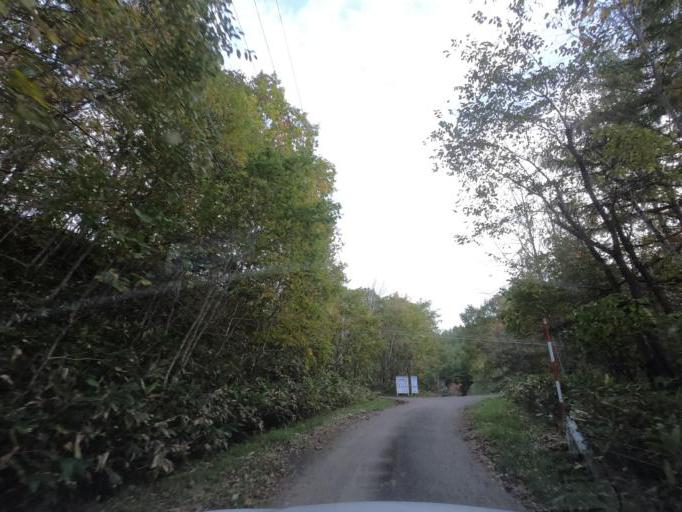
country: JP
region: Hokkaido
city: Obihiro
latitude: 42.5872
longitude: 143.3148
